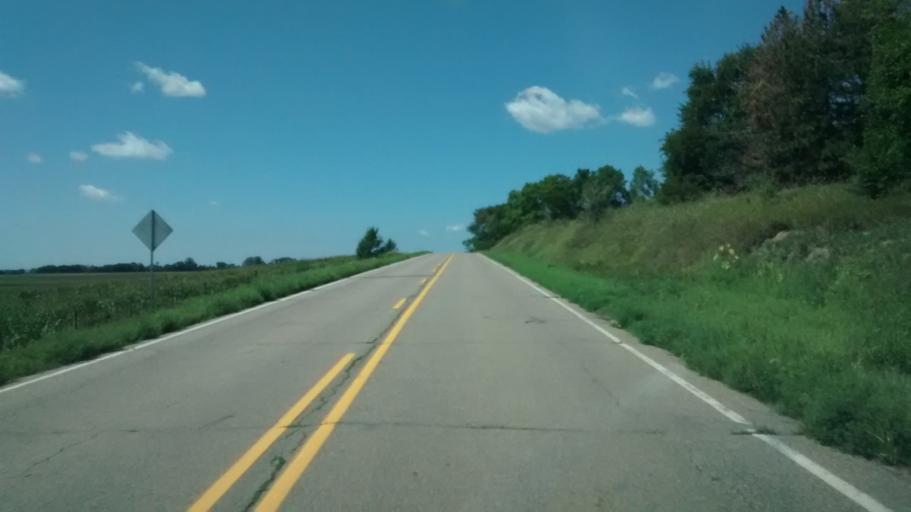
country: US
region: Iowa
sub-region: Woodbury County
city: Moville
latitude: 42.2683
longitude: -96.0645
